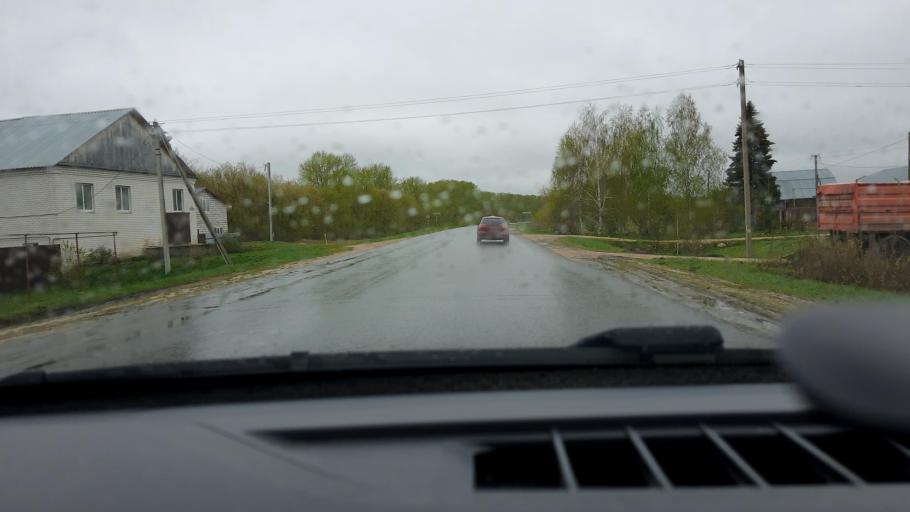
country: RU
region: Nizjnij Novgorod
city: Perevoz
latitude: 55.5895
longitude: 44.6365
